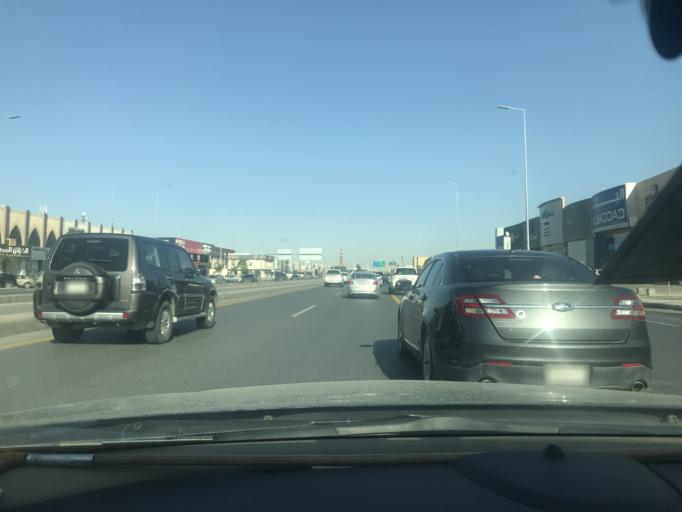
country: SA
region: Ar Riyad
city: Riyadh
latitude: 24.7260
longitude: 46.6908
